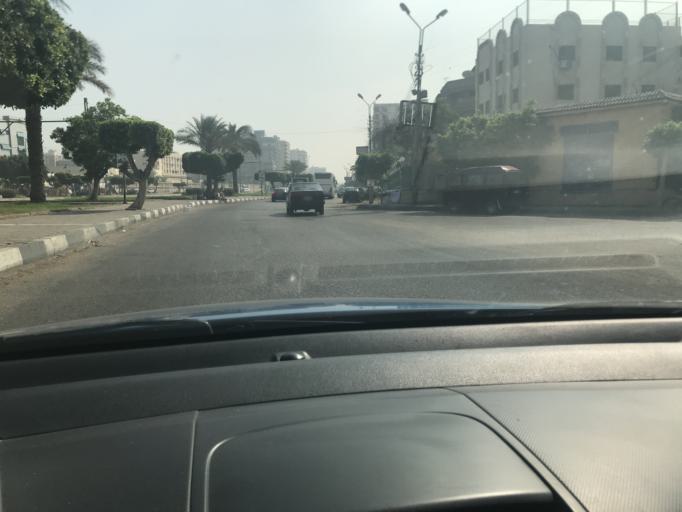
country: EG
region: Muhafazat al Qalyubiyah
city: Al Khankah
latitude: 30.1114
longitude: 31.3463
